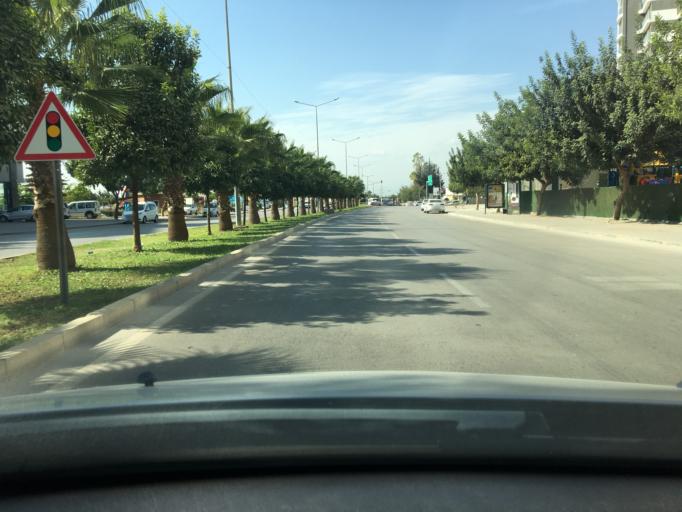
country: TR
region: Adana
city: Seyhan
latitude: 37.0230
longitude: 35.2558
